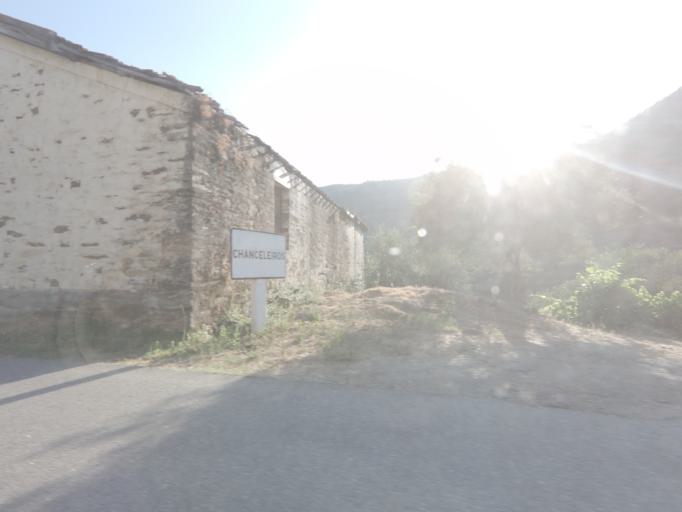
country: PT
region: Vila Real
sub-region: Sabrosa
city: Vilela
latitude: 41.1769
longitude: -7.5794
